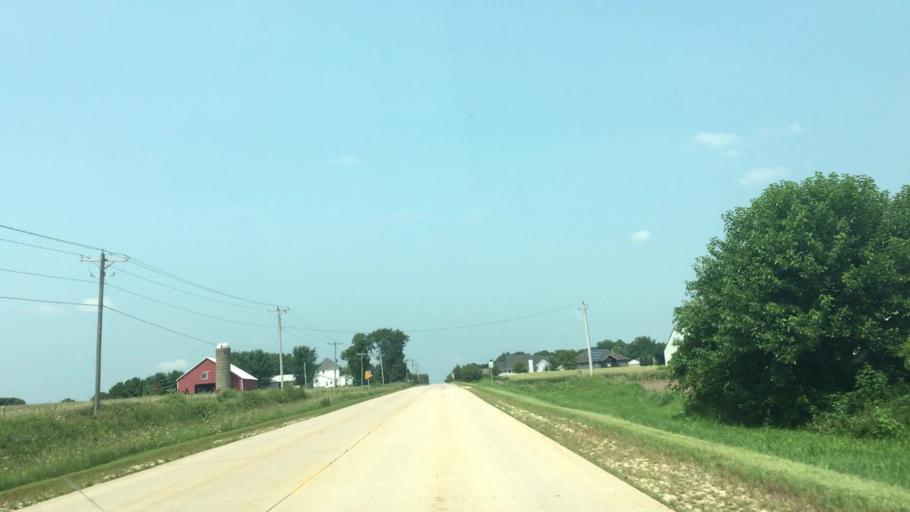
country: US
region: Iowa
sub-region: Fayette County
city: Oelwein
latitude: 42.6716
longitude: -91.8937
